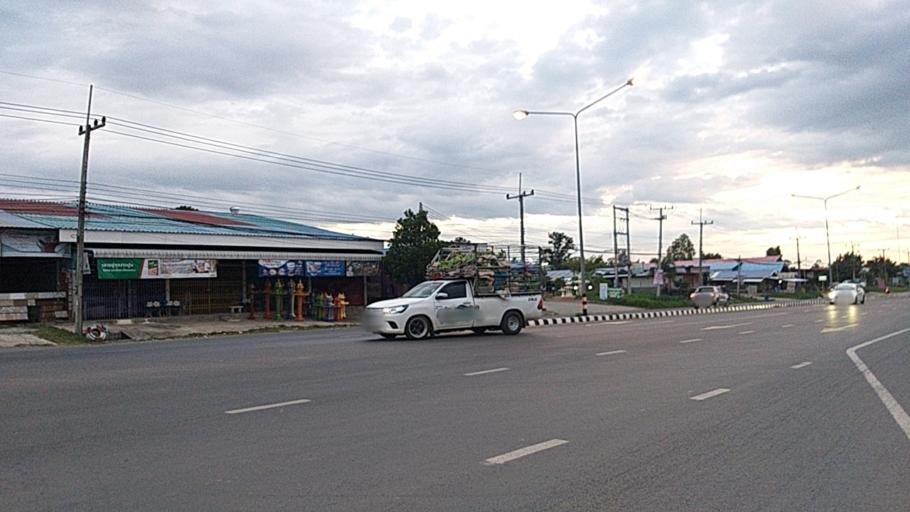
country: TH
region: Surin
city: Kap Choeng
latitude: 14.4522
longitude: 103.6954
